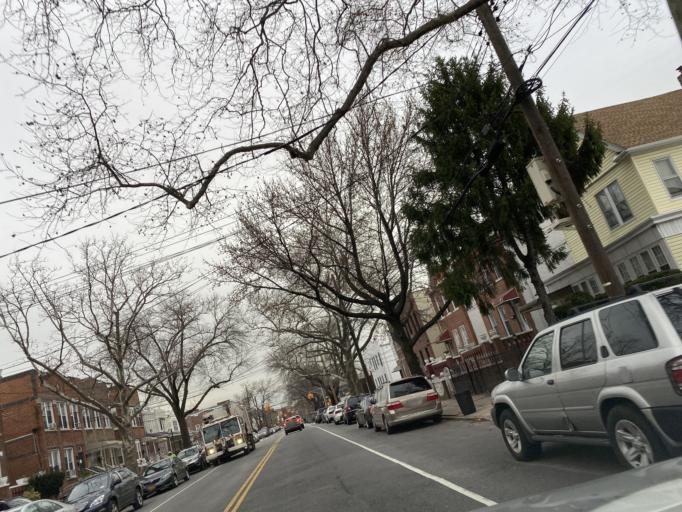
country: US
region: New York
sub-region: Kings County
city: Brooklyn
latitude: 40.6539
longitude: -73.9393
